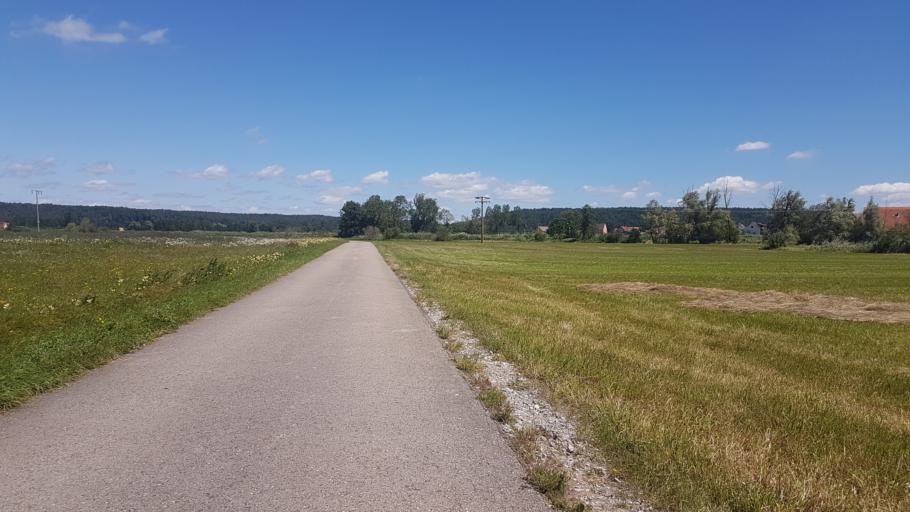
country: DE
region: Bavaria
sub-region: Regierungsbezirk Mittelfranken
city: Aurach
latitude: 49.2604
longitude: 10.4514
